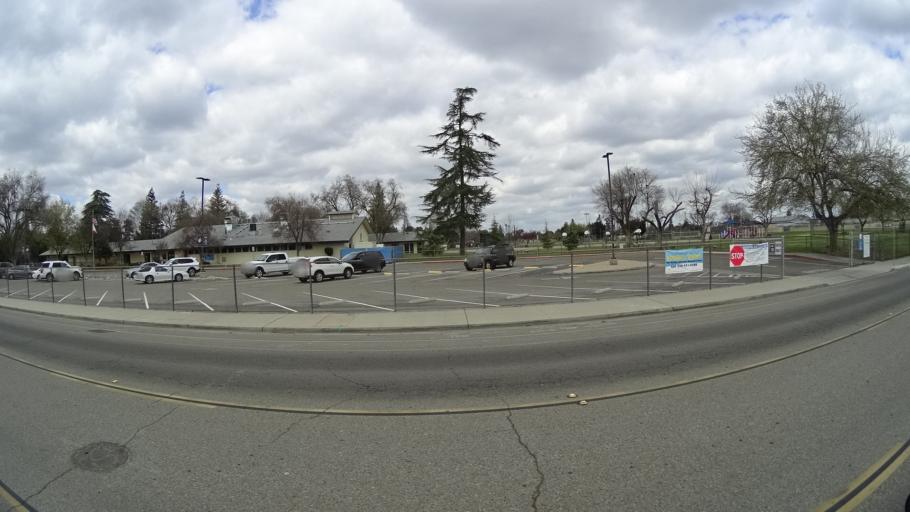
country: US
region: California
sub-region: Fresno County
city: Fresno
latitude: 36.8155
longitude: -119.8141
